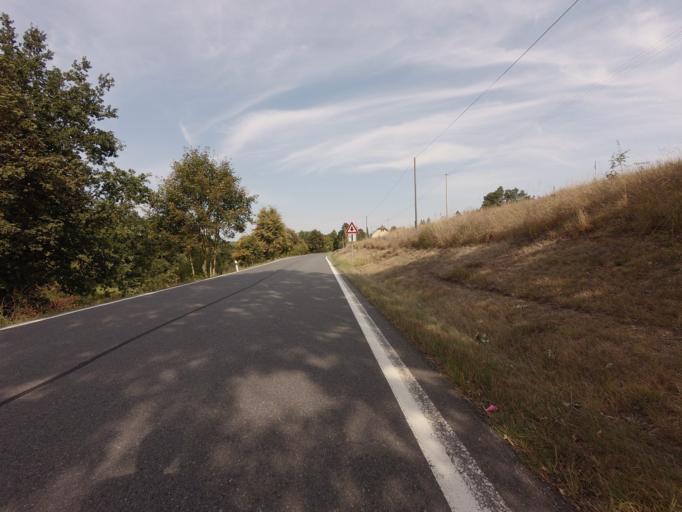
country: CZ
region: Central Bohemia
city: Petrovice
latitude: 49.5411
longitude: 14.3492
